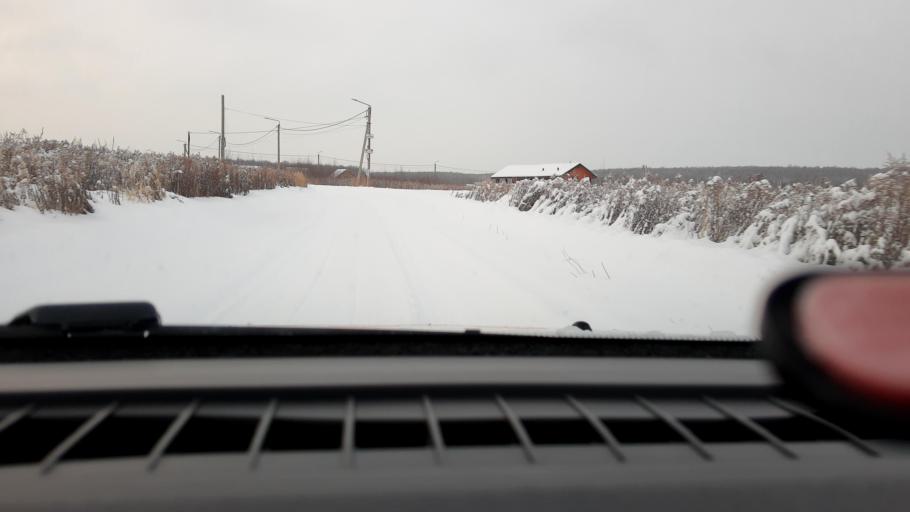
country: RU
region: Nizjnij Novgorod
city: Afonino
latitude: 56.1334
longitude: 43.9887
